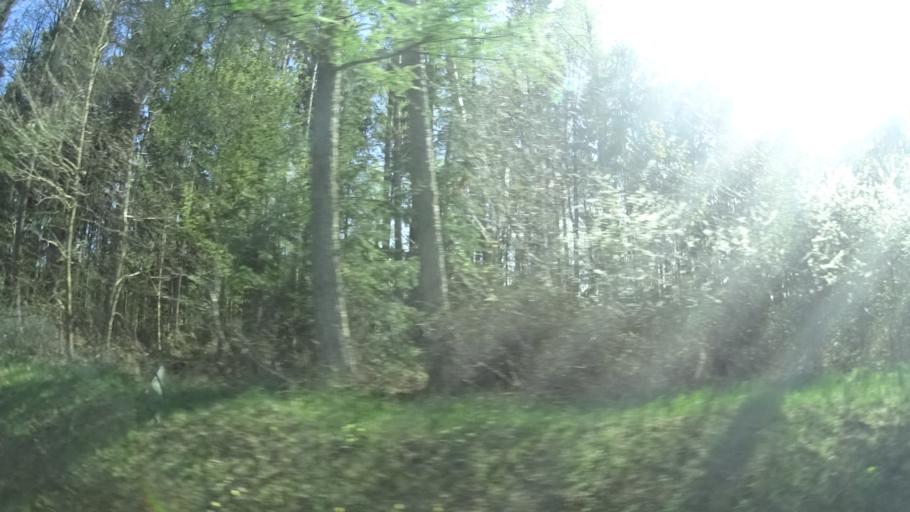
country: DE
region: Bavaria
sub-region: Regierungsbezirk Unterfranken
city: Burgpreppach
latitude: 50.1367
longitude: 10.5935
